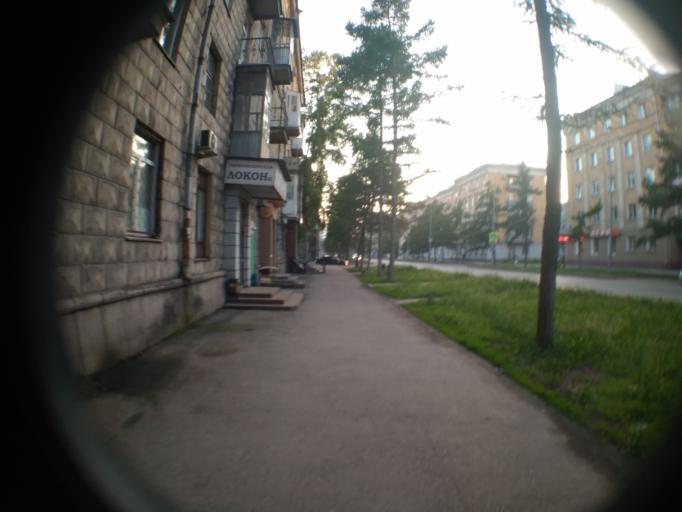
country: RU
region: Kemerovo
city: Novokuznetsk
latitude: 53.7546
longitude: 87.1154
